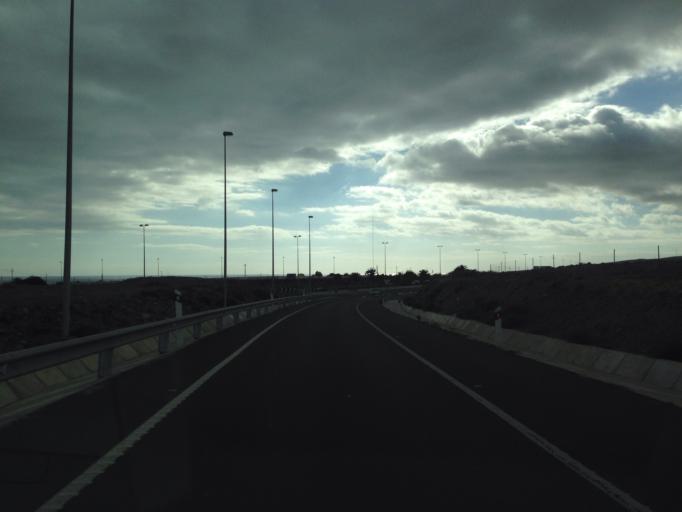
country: ES
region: Canary Islands
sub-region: Provincia de Las Palmas
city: Cruce de Arinaga
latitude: 27.8246
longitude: -15.4583
